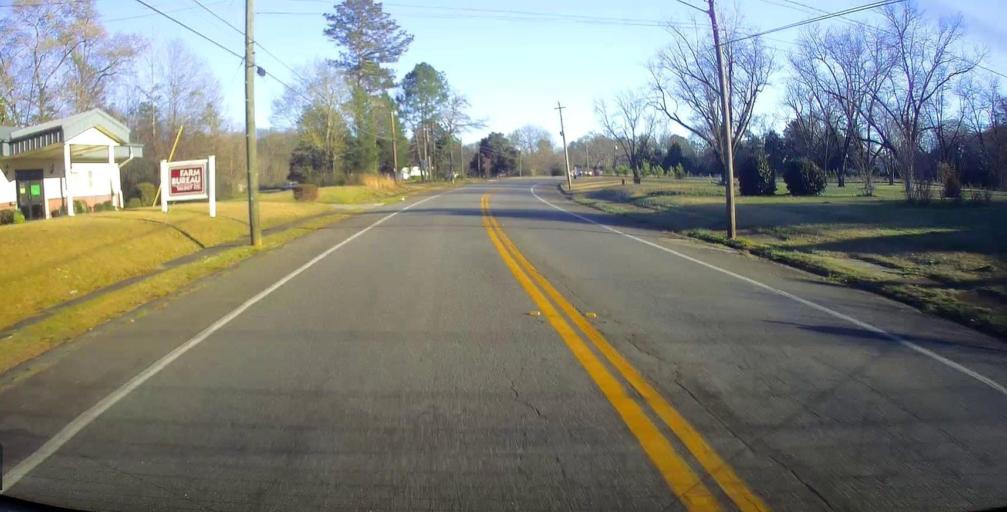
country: US
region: Georgia
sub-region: Talbot County
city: Talbotton
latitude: 32.6688
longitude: -84.5346
